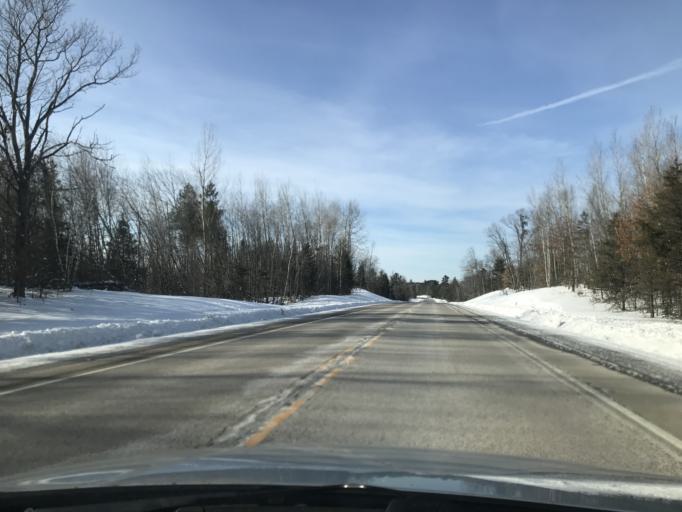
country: US
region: Wisconsin
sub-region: Oconto County
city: Gillett
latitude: 45.1239
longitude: -88.3970
